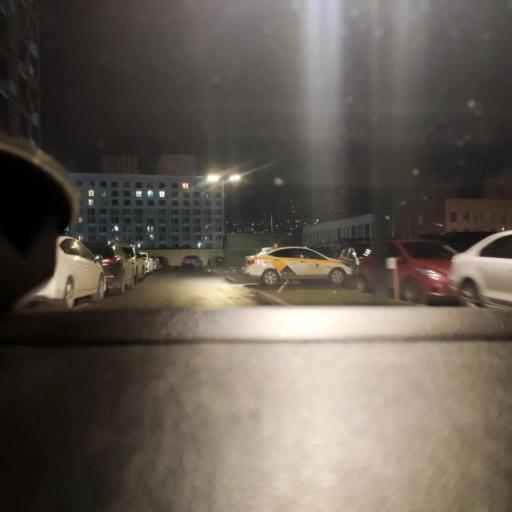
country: RU
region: Moscow
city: Nekrasovka
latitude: 55.6999
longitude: 37.9092
